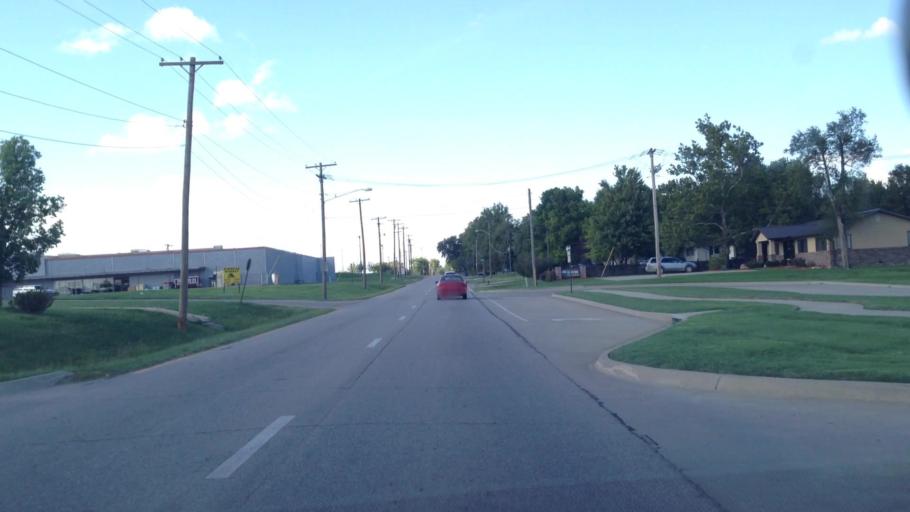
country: US
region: Kansas
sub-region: Franklin County
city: Ottawa
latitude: 38.5830
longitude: -95.2677
